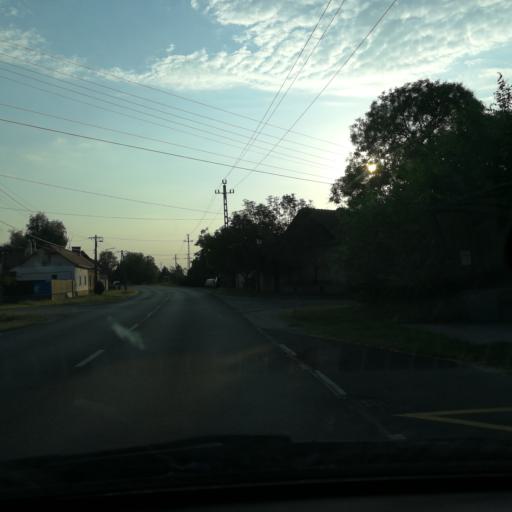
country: HU
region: Bacs-Kiskun
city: Kiskunmajsa
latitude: 46.4931
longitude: 19.7257
